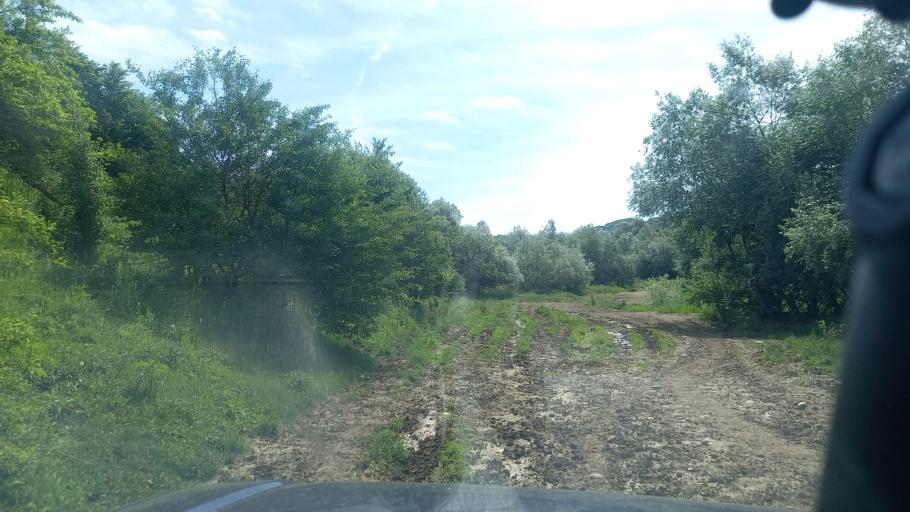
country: RU
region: Karachayevo-Cherkesiya
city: Kurdzhinovo
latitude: 44.1406
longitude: 41.0667
